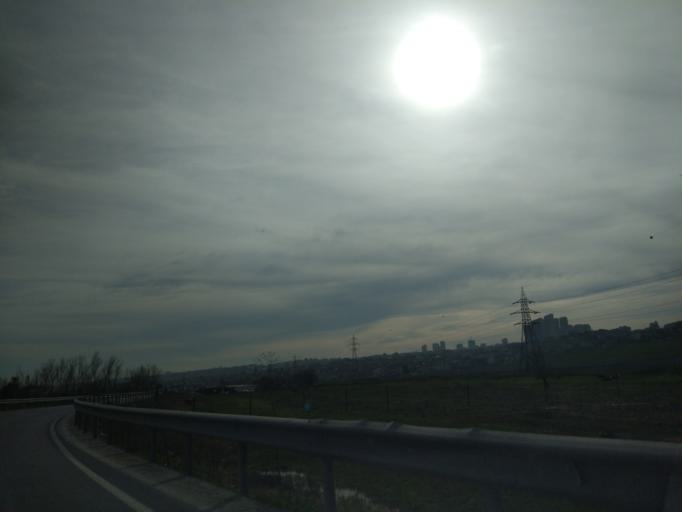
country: TR
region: Istanbul
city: Esenyurt
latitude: 41.0551
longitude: 28.7020
